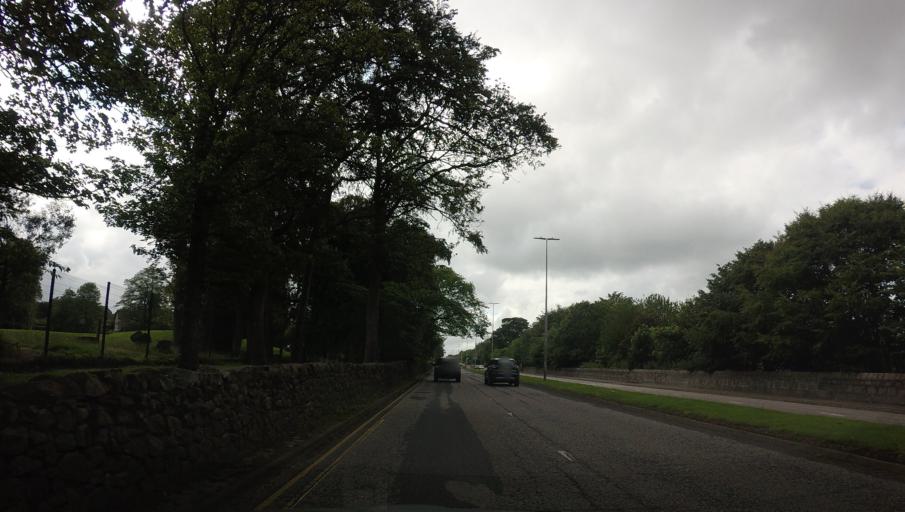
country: GB
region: Scotland
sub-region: Aberdeen City
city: Aberdeen
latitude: 57.1521
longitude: -2.1401
